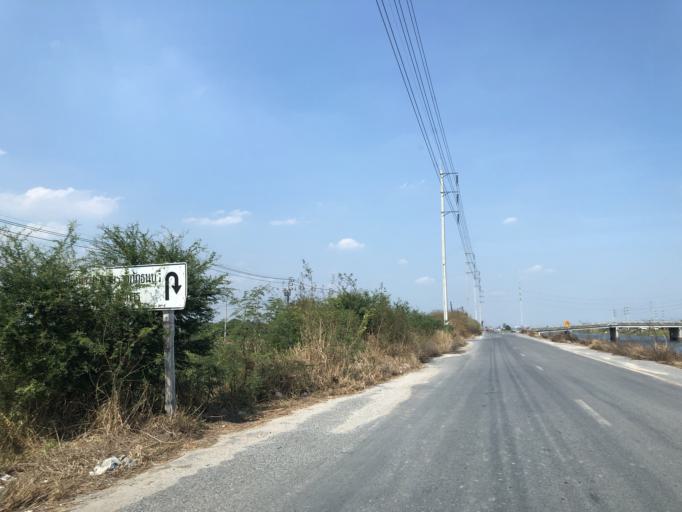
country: TH
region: Samut Prakan
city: Bang Bo District
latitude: 13.5249
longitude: 100.7476
